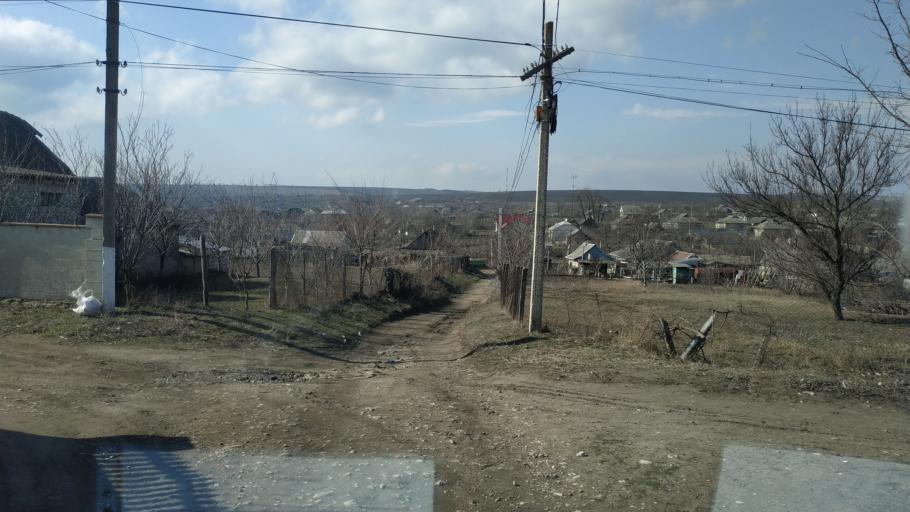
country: MD
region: Basarabeasca
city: Basarabeasca
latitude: 46.5762
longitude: 29.1184
